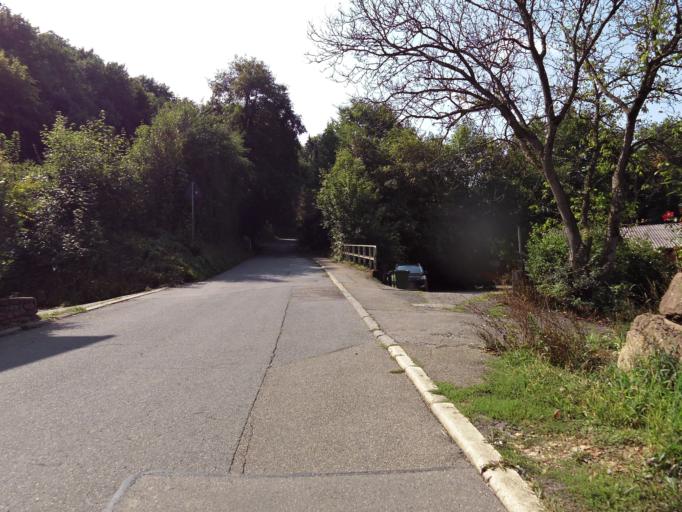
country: DE
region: Baden-Wuerttemberg
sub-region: Karlsruhe Region
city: Eschelbronn
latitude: 49.3335
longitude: 8.8519
